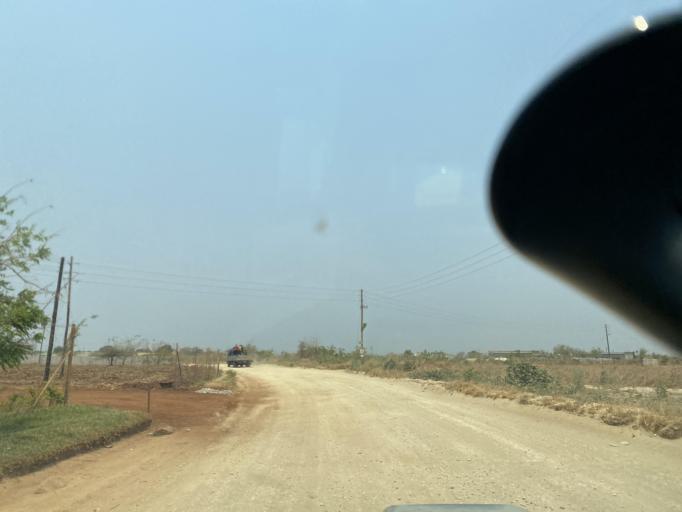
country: ZM
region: Lusaka
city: Lusaka
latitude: -15.5391
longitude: 28.3503
